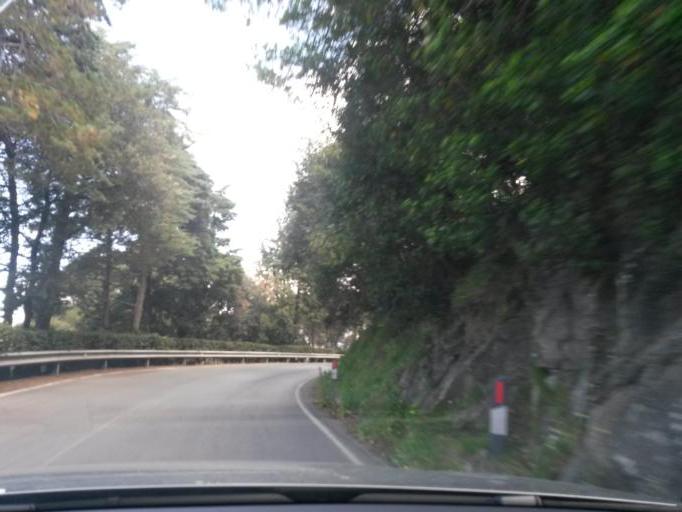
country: IT
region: Tuscany
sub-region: Provincia di Livorno
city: Marciana Marina
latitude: 42.7932
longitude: 10.2181
